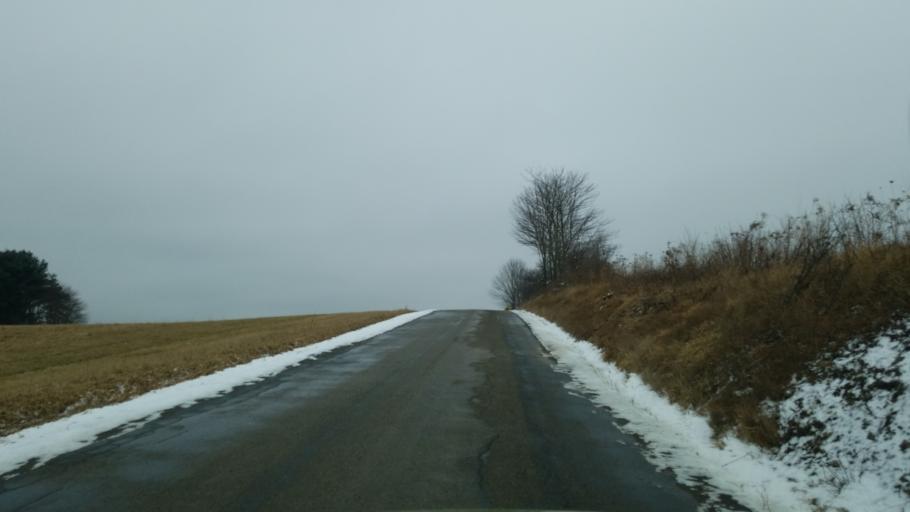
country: US
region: Pennsylvania
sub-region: Jefferson County
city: Reynoldsville
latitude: 41.0857
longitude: -78.8499
